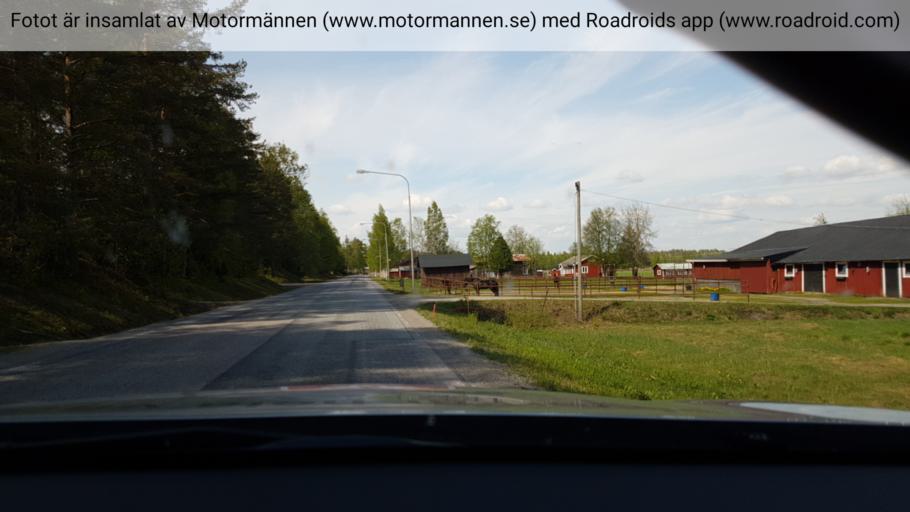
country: SE
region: Vaesterbotten
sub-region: Umea Kommun
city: Roback
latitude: 63.8119
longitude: 20.1911
